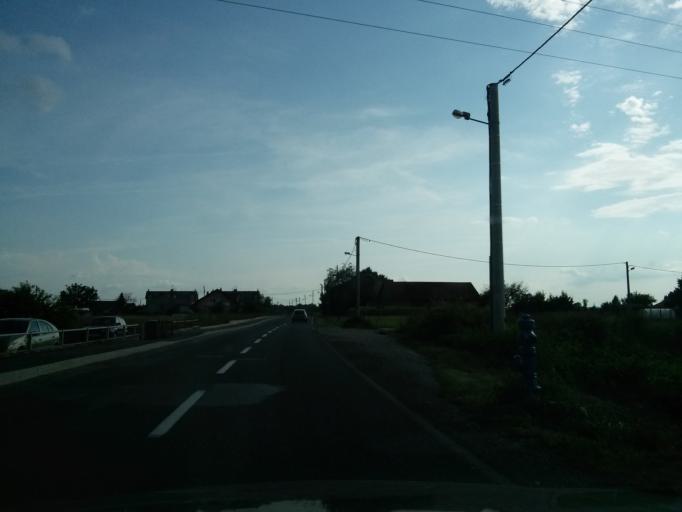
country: HR
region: Grad Zagreb
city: Zadvorsko
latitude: 45.7539
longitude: 15.9280
